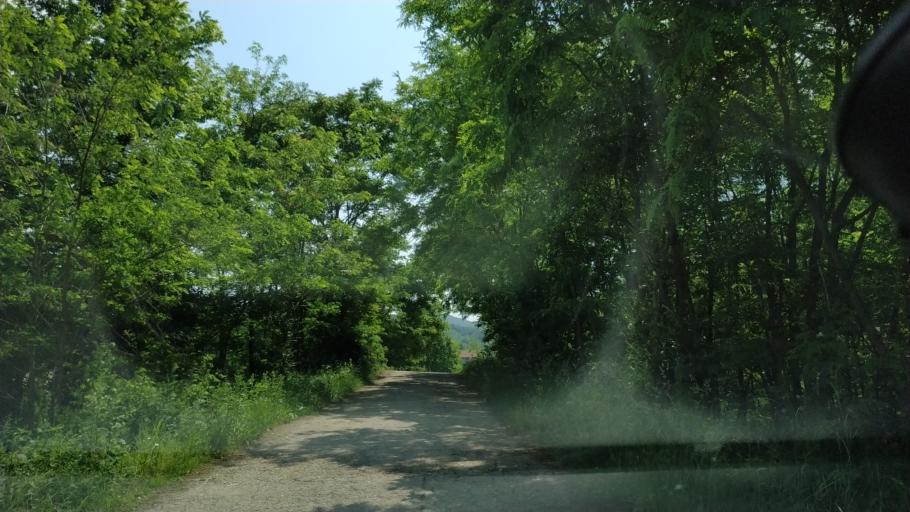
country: RS
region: Central Serbia
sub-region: Nisavski Okrug
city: Aleksinac
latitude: 43.4220
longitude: 21.7183
